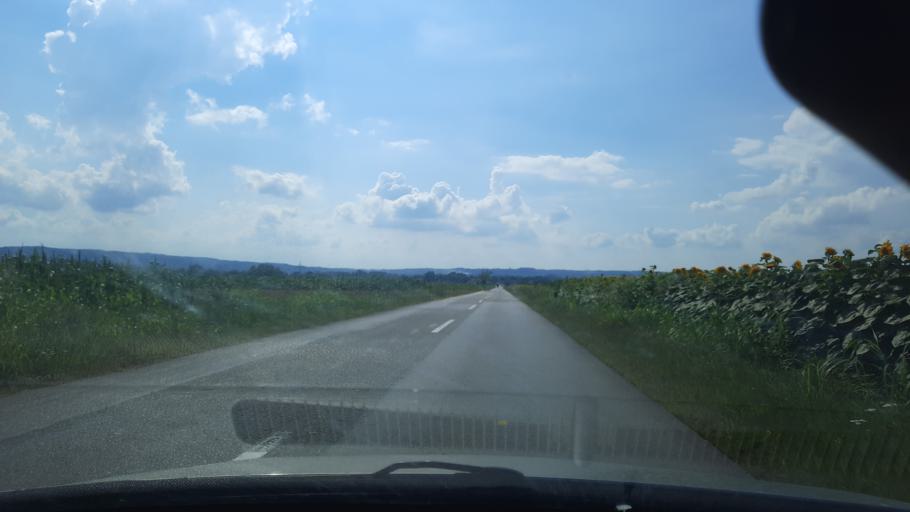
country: RS
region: Central Serbia
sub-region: Branicevski Okrug
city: Malo Crnice
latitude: 44.5853
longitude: 21.2911
